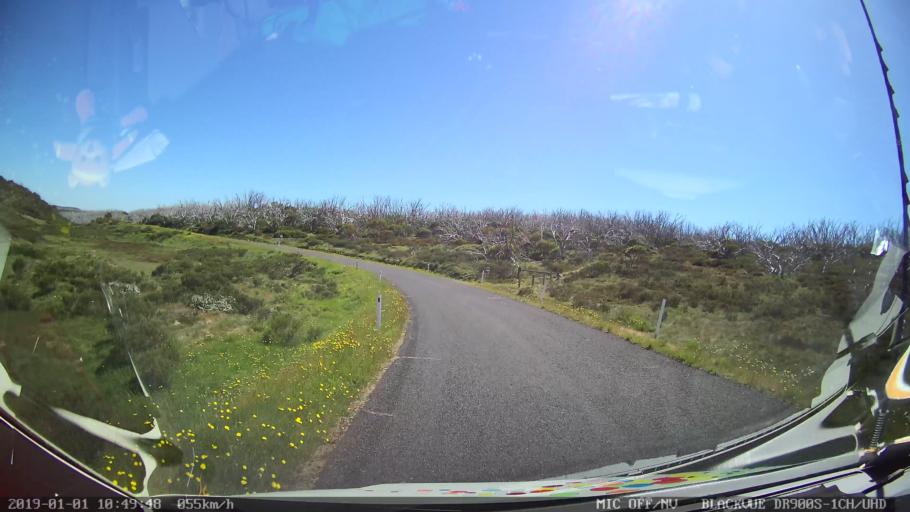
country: AU
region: New South Wales
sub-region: Snowy River
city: Jindabyne
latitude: -36.0336
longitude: 148.3739
